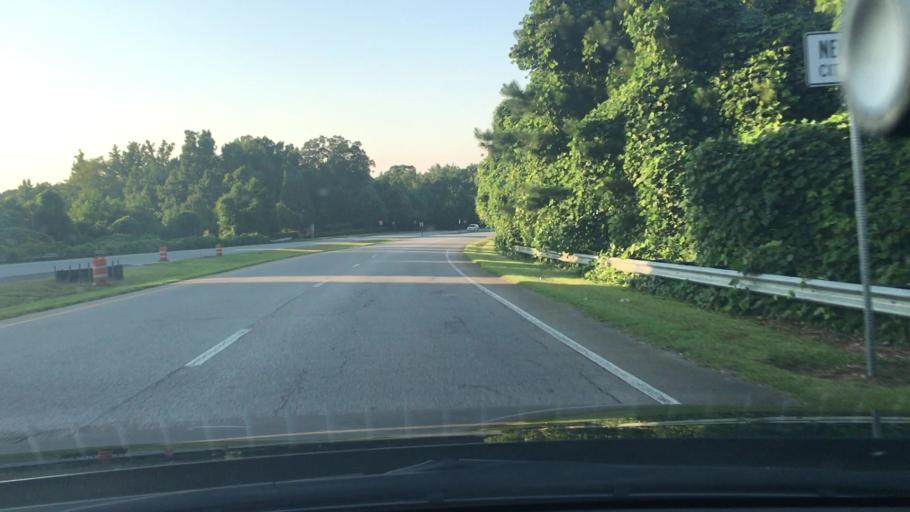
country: US
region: Georgia
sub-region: Coweta County
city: East Newnan
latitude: 33.3640
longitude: -84.7656
